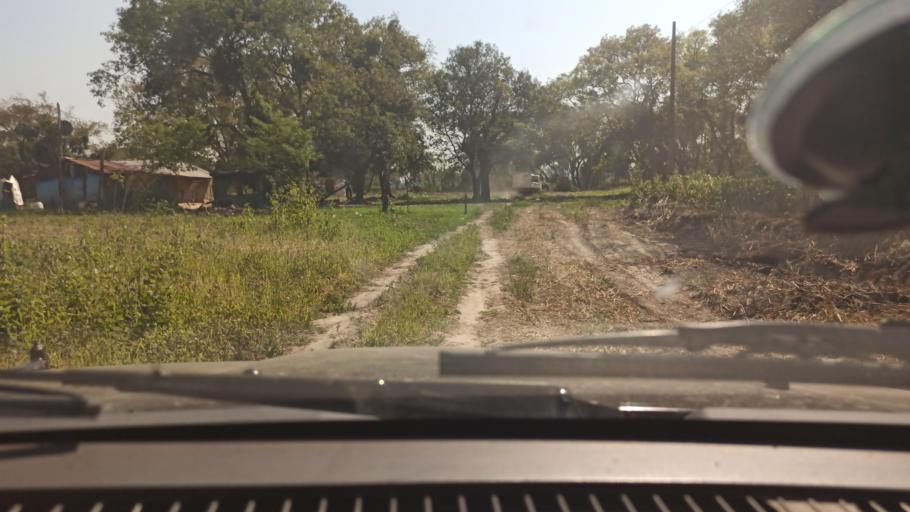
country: PY
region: Asuncion
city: Asuncion
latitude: -25.3507
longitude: -57.6707
